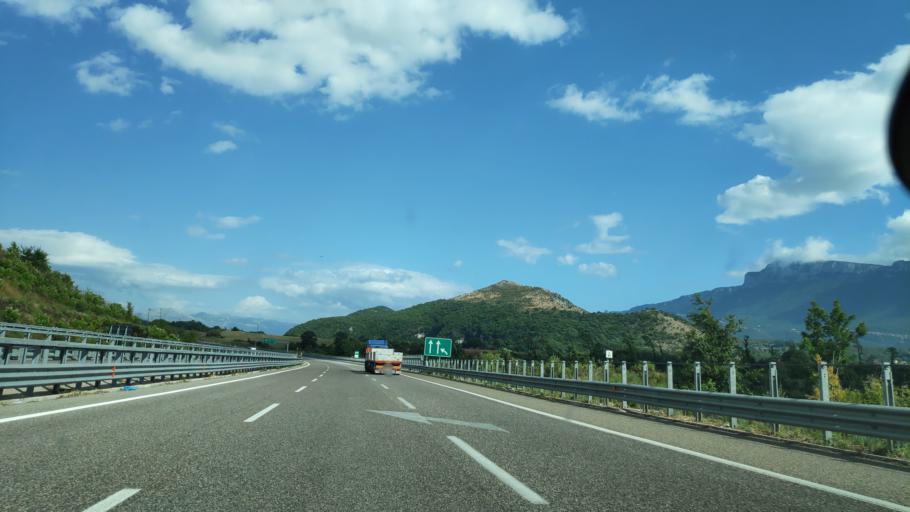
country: IT
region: Campania
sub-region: Provincia di Salerno
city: Palomonte
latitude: 40.6122
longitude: 15.2823
